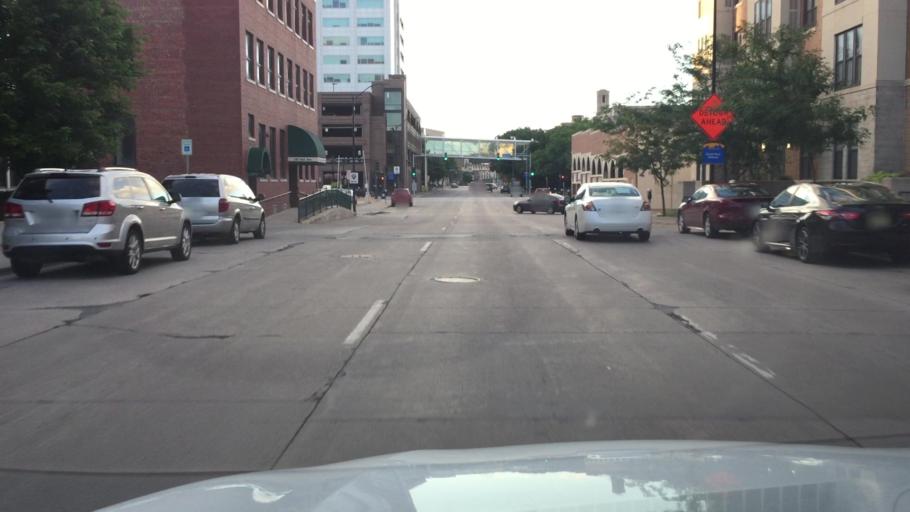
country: US
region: Iowa
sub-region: Polk County
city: Des Moines
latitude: 41.5845
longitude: -93.6189
